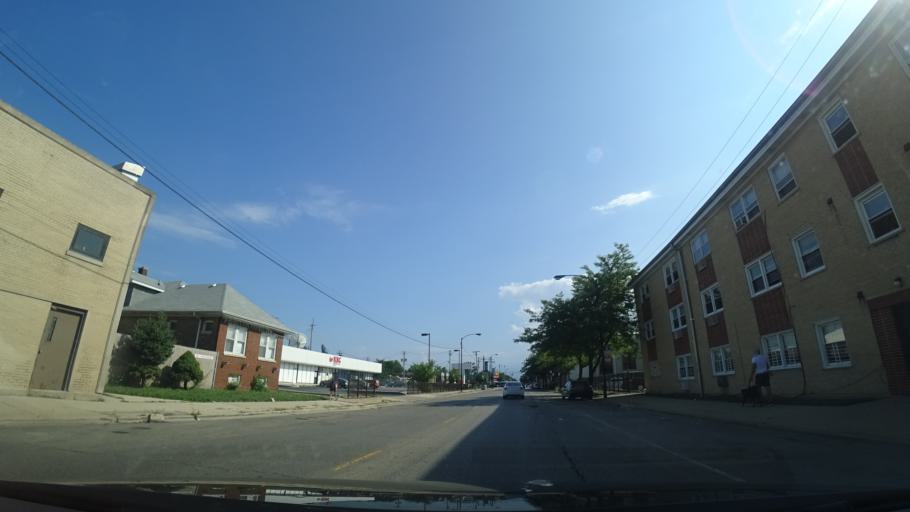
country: US
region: Illinois
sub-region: Cook County
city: Lincolnwood
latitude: 41.9775
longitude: -87.7089
